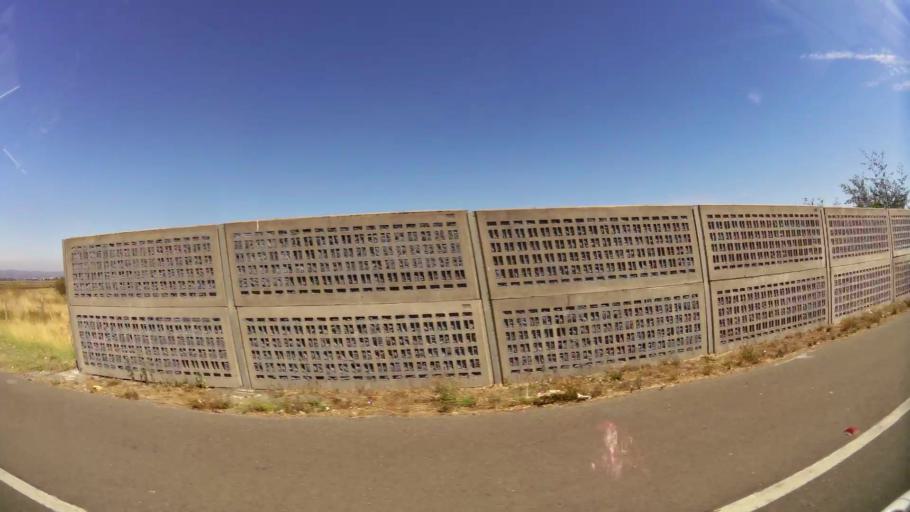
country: CL
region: Biobio
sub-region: Provincia de Concepcion
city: Talcahuano
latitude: -36.7317
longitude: -73.0944
